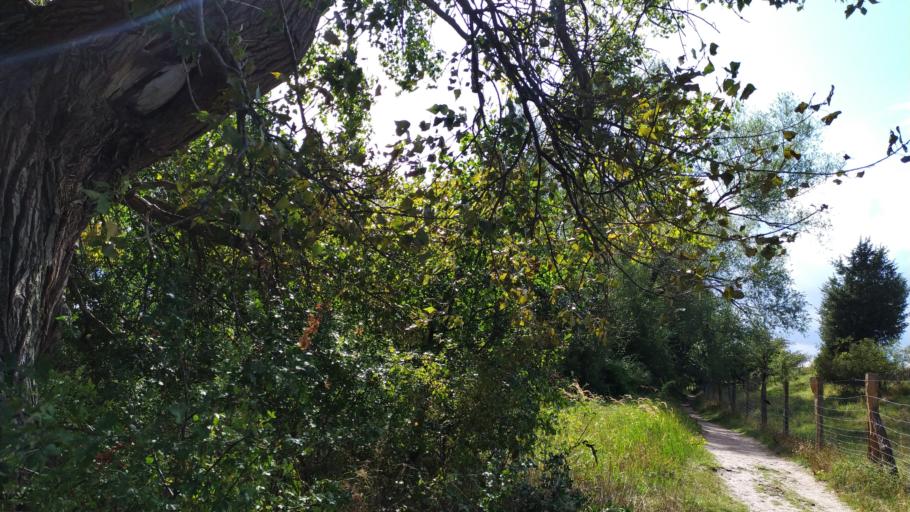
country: DE
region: Mecklenburg-Vorpommern
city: Lassan
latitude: 54.0048
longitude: 13.8635
